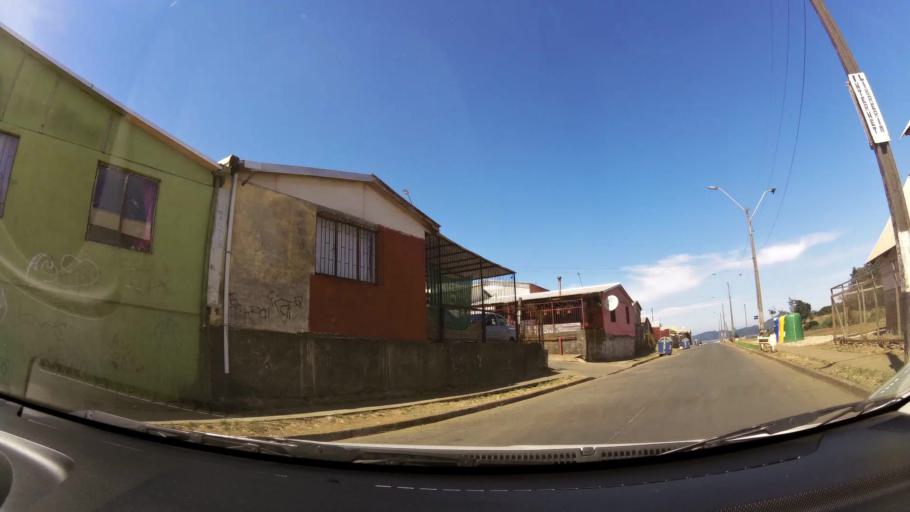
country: CL
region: Biobio
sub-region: Provincia de Concepcion
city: Talcahuano
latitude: -36.7132
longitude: -73.1401
